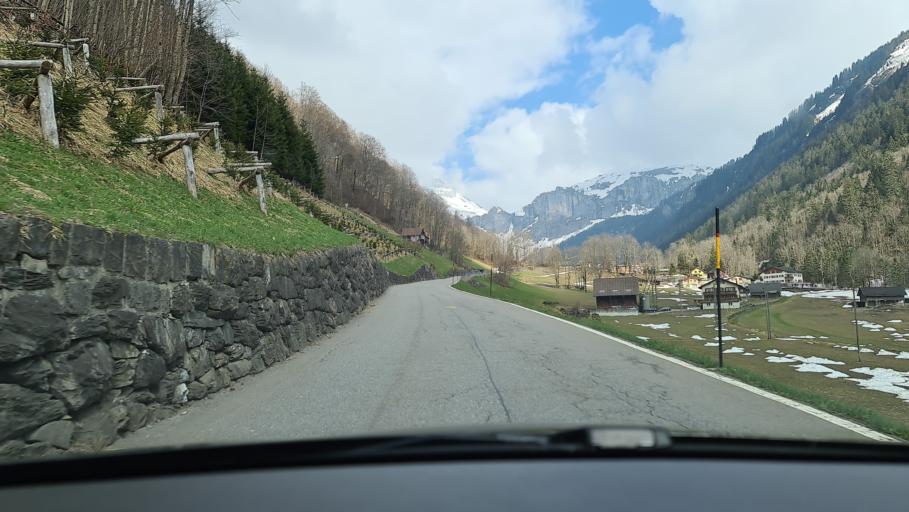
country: CH
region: Uri
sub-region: Uri
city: Burglen
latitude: 46.8646
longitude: 8.7736
